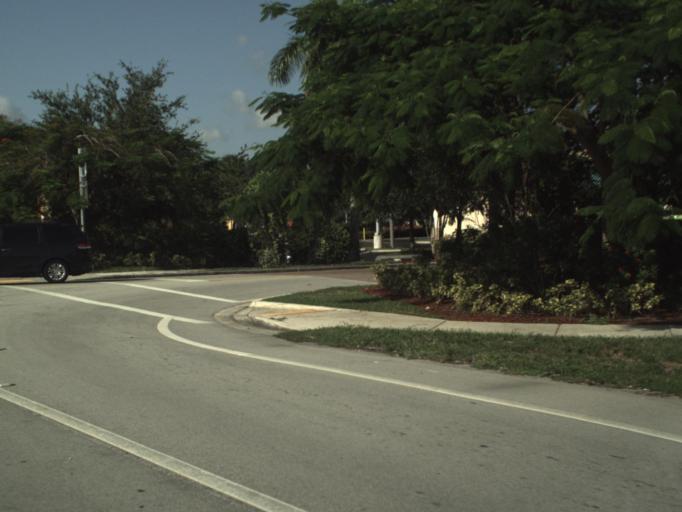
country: US
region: Florida
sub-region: Broward County
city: Coconut Creek
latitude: 26.2853
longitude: -80.2021
